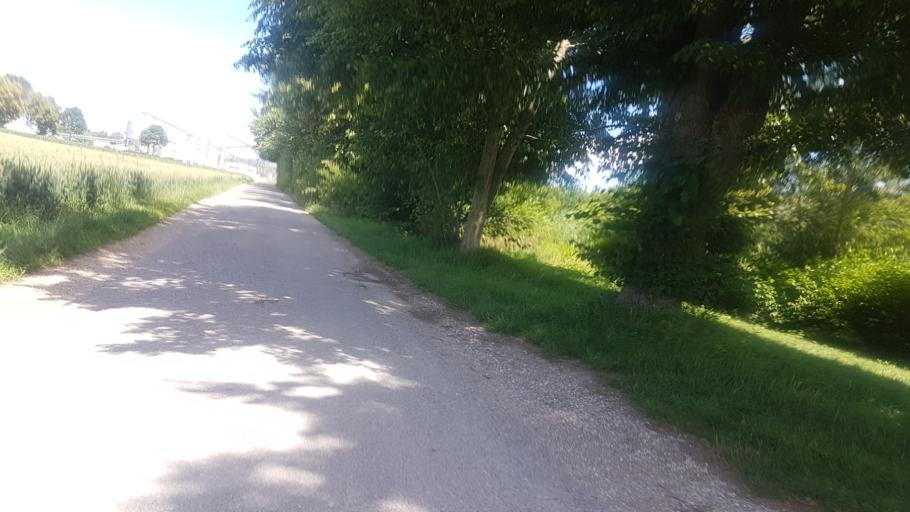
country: DE
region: Bavaria
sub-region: Swabia
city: Hochstadt an der Donau
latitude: 48.6060
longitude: 10.5776
